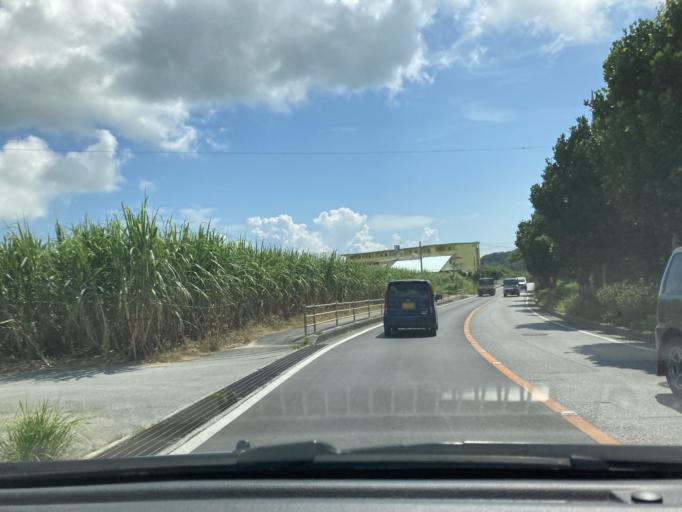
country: JP
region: Okinawa
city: Tomigusuku
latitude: 26.1532
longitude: 127.7761
